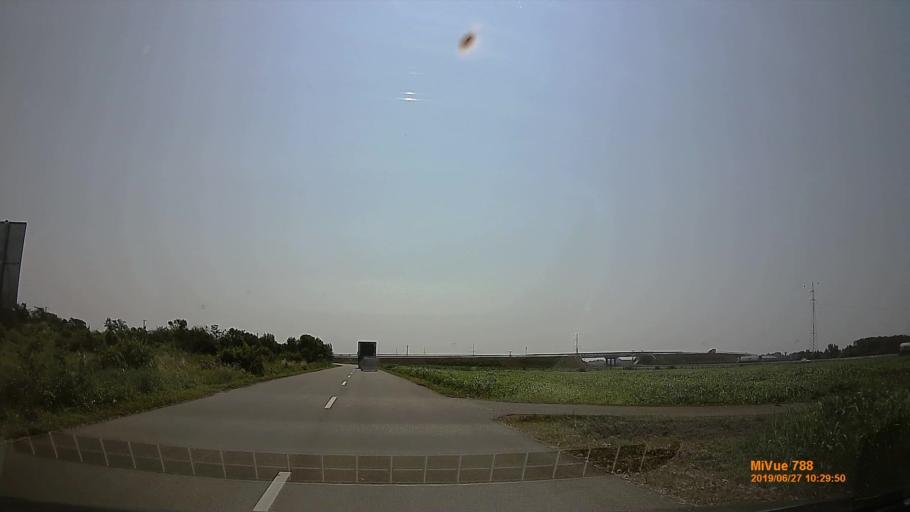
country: HU
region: Pest
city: Cegled
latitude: 47.2041
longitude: 19.7811
